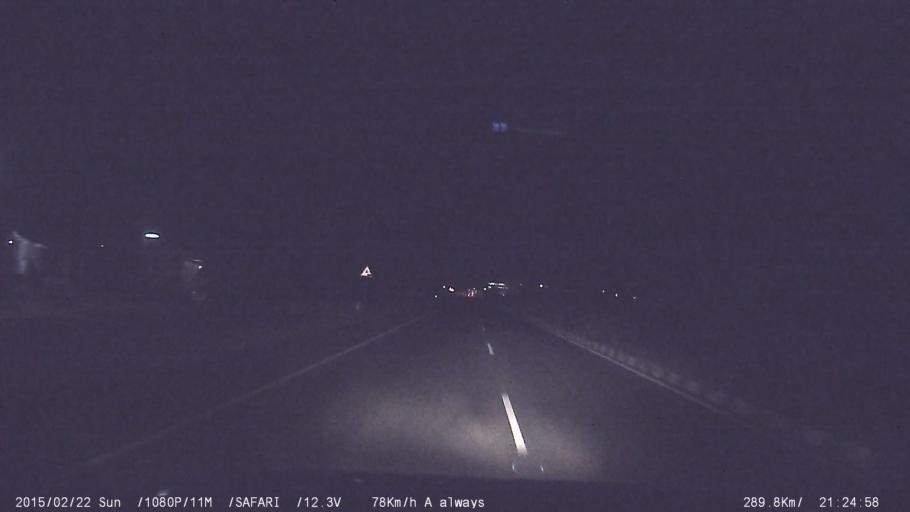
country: IN
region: Tamil Nadu
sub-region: Karur
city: Karur
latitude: 10.8925
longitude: 78.0233
